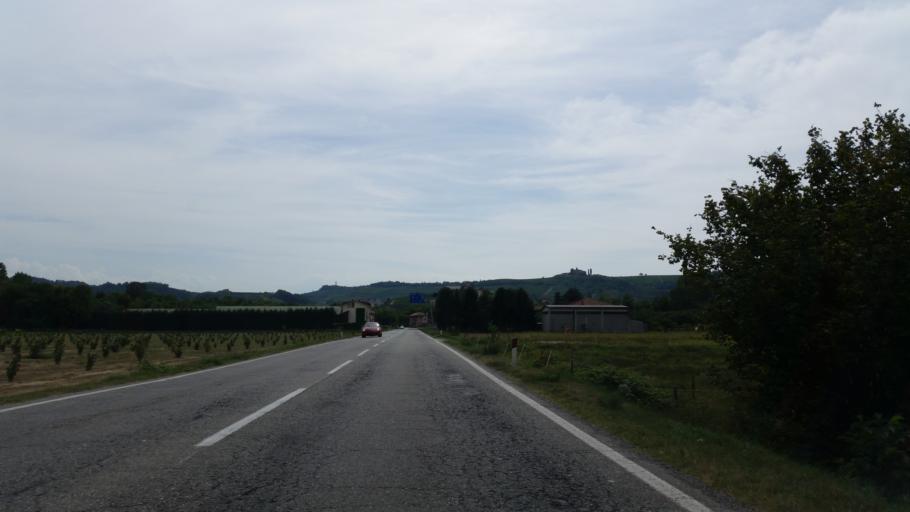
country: IT
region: Piedmont
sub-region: Provincia di Cuneo
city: Castiglione Falletto
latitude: 44.6298
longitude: 7.9597
